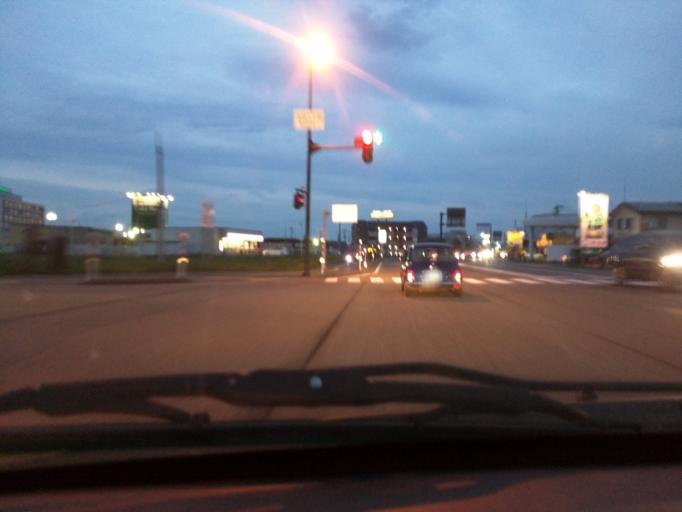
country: JP
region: Niigata
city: Kashiwazaki
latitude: 37.3634
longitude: 138.5815
